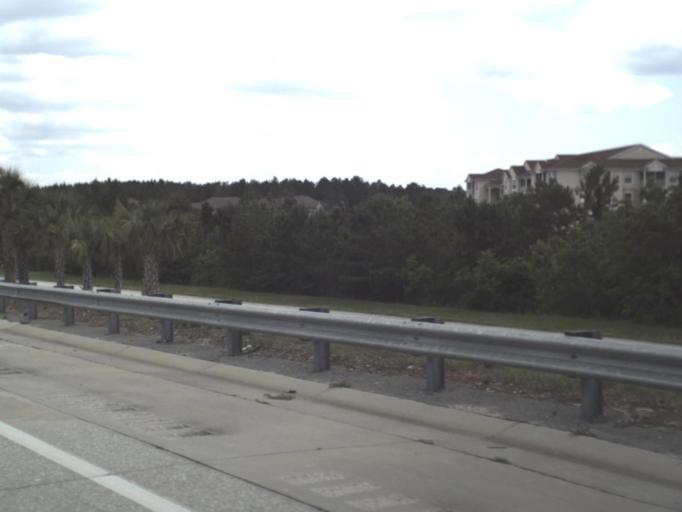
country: US
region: Florida
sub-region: Saint Johns County
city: Ponte Vedra Beach
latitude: 30.2337
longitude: -81.5144
